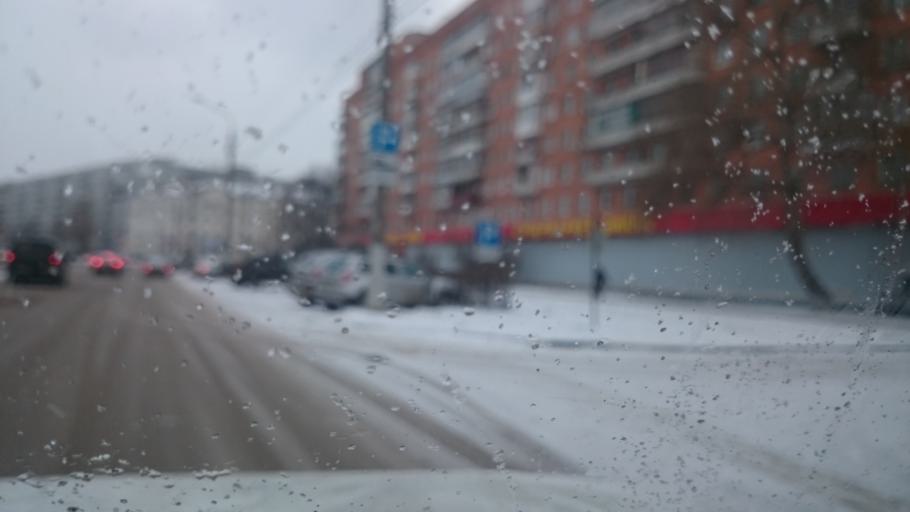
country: RU
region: Tula
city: Tula
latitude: 54.1985
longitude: 37.6015
